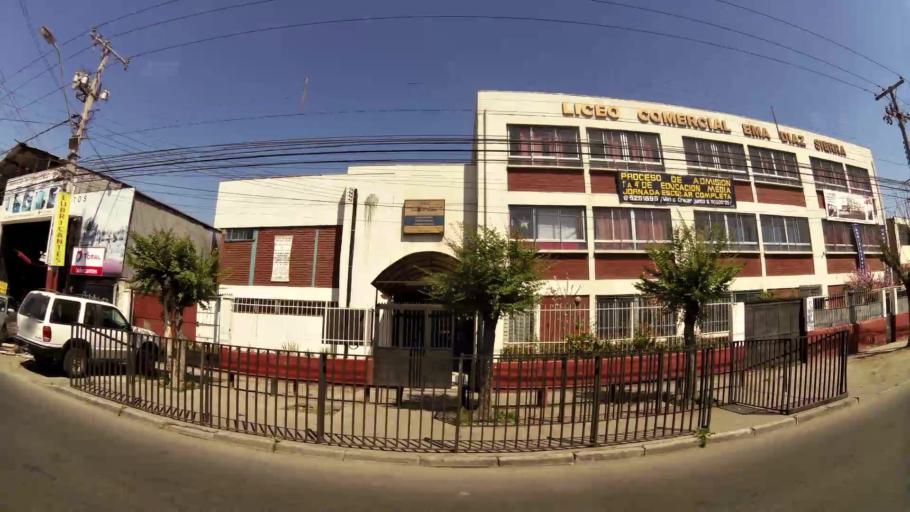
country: CL
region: Santiago Metropolitan
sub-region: Provincia de Santiago
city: La Pintana
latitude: -33.5295
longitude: -70.6423
